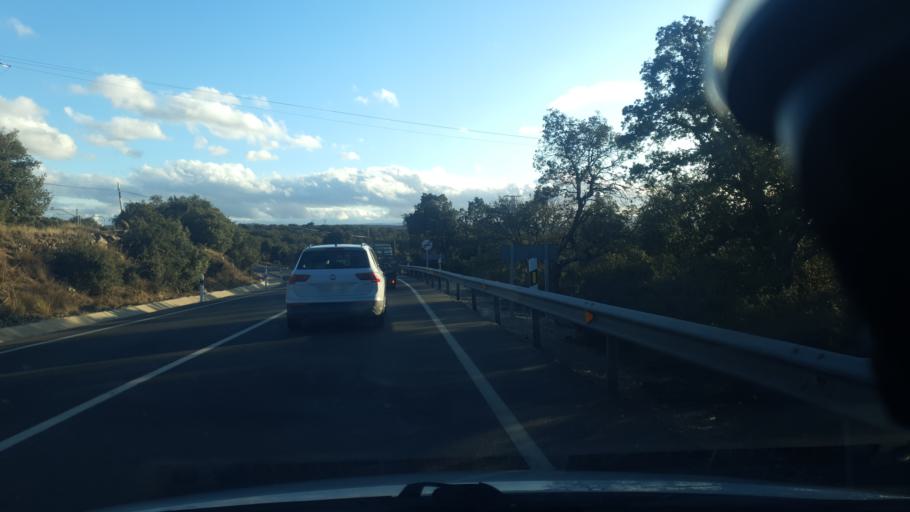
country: ES
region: Castille and Leon
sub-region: Provincia de Avila
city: Mingorria
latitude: 40.7167
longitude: -4.6743
